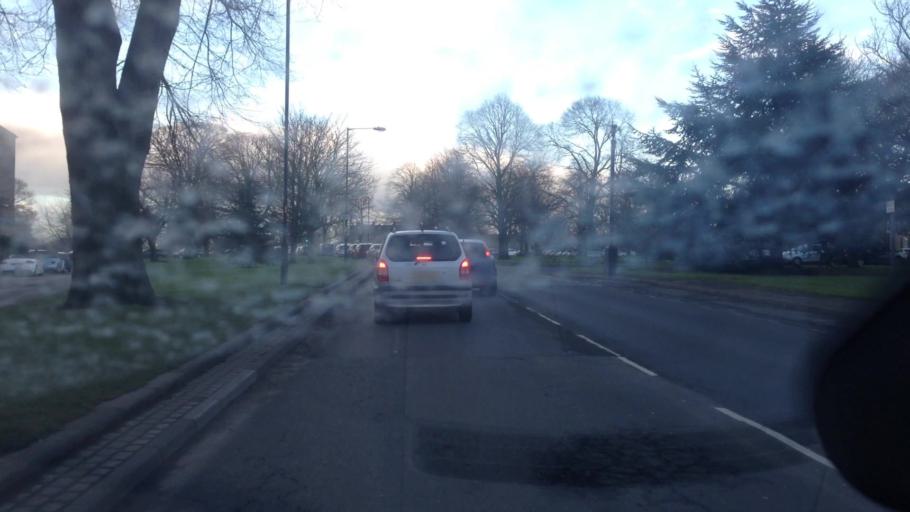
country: GB
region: England
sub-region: North Yorkshire
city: Harrogate
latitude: 53.9974
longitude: -1.5286
